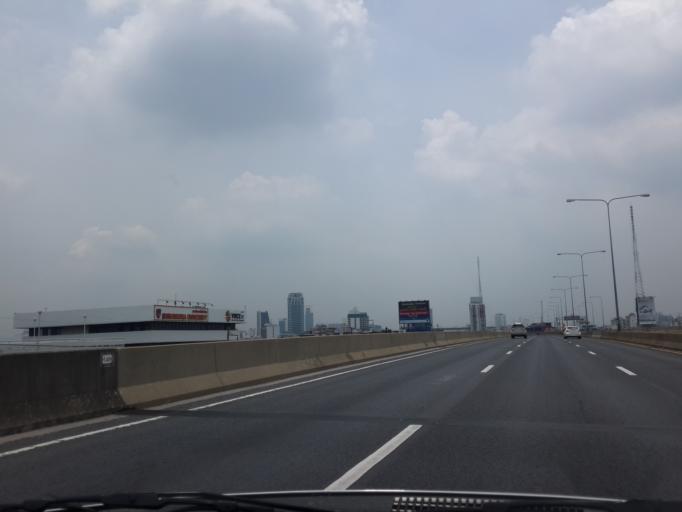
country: TH
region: Bangkok
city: Din Daeng
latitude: 13.7840
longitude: 100.5591
